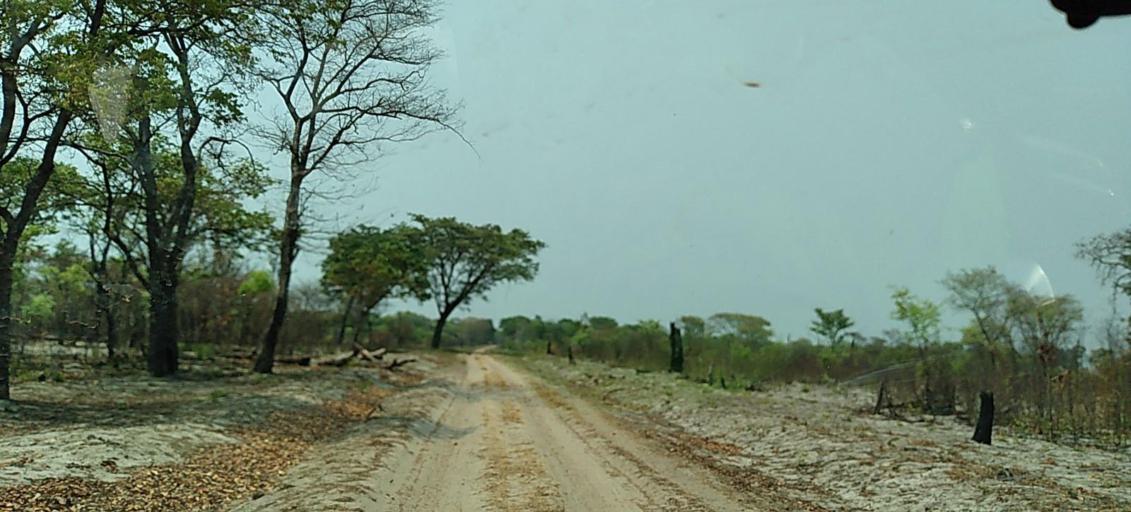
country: ZM
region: North-Western
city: Zambezi
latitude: -13.9449
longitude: 23.2231
